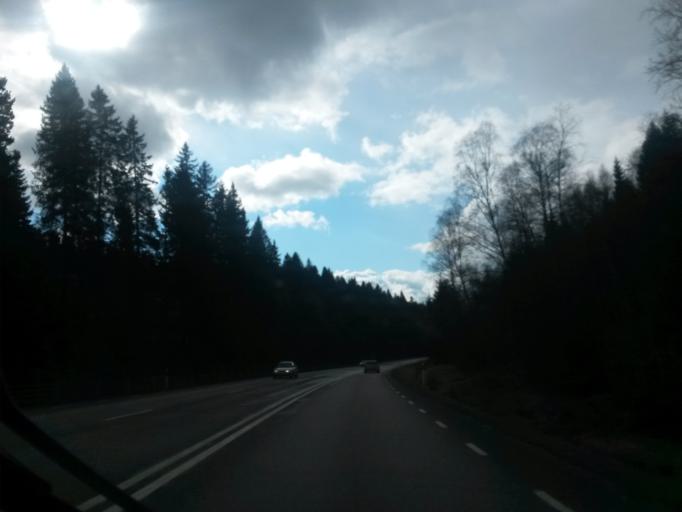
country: SE
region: Vaestra Goetaland
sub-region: Skovde Kommun
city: Skultorp
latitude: 58.3774
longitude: 13.7147
